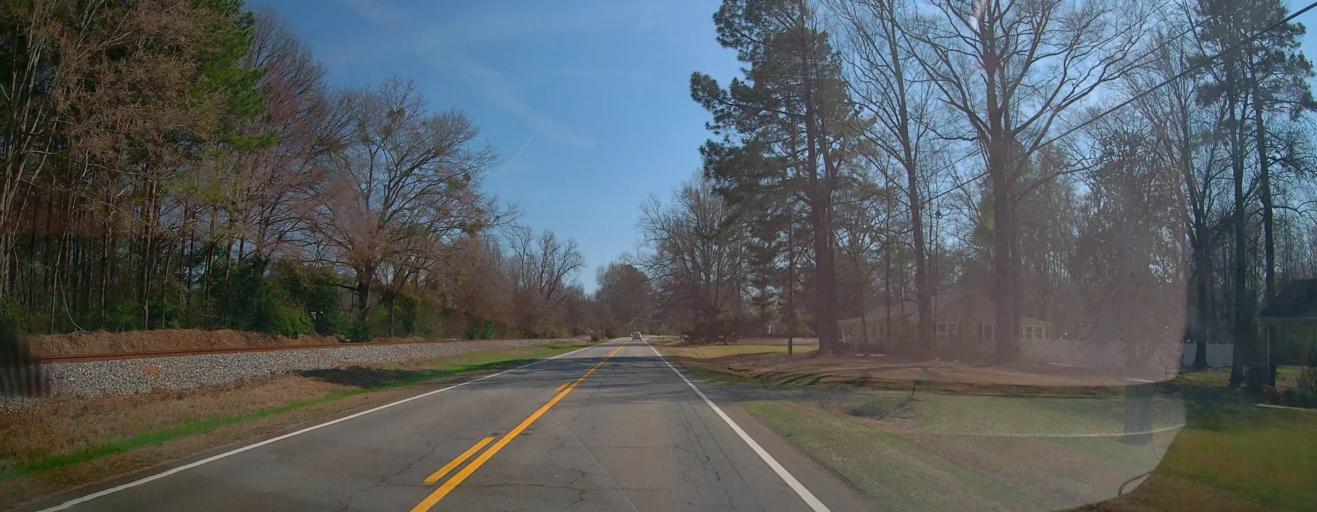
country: US
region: Georgia
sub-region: Jones County
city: Gray
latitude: 33.0165
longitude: -83.5352
